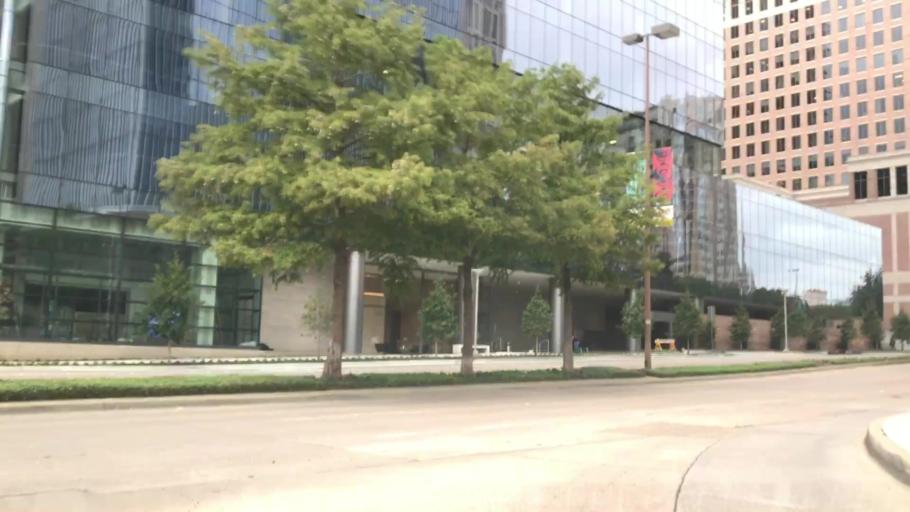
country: US
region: Texas
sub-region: Dallas County
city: Dallas
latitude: 32.7910
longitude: -96.8006
